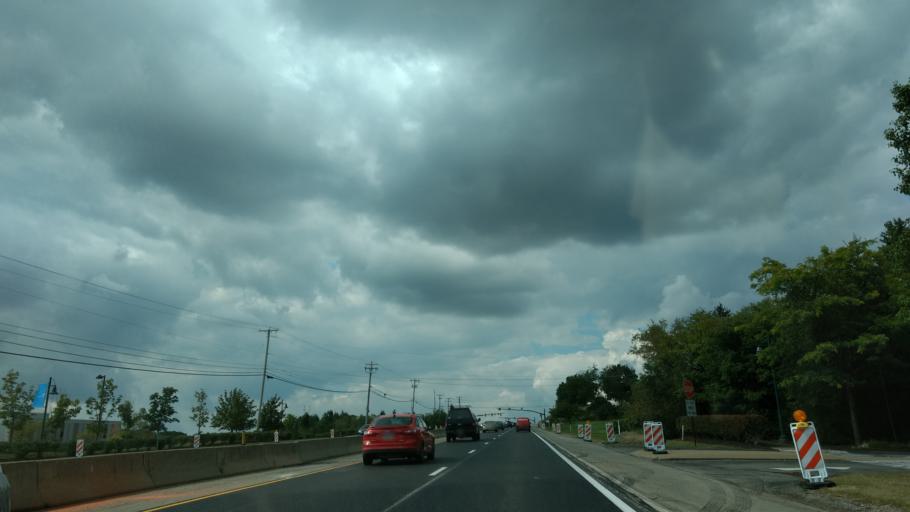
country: US
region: Pennsylvania
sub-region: Allegheny County
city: Bradford Woods
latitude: 40.6353
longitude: -80.0611
